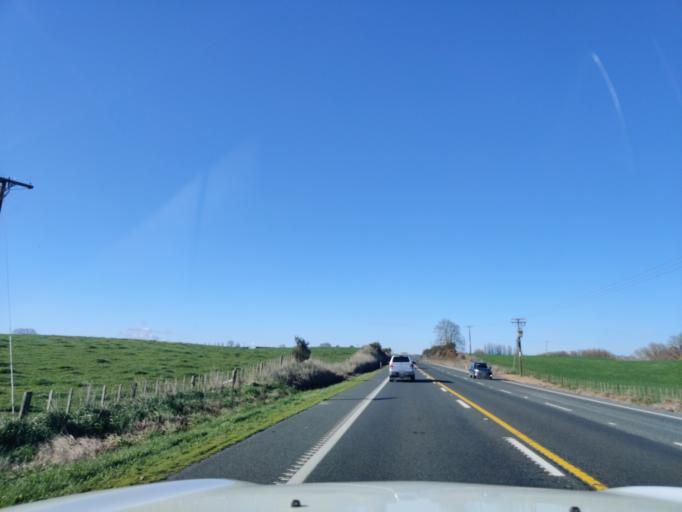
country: NZ
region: Waikato
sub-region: Matamata-Piako District
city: Matamata
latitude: -38.0219
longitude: 175.7842
